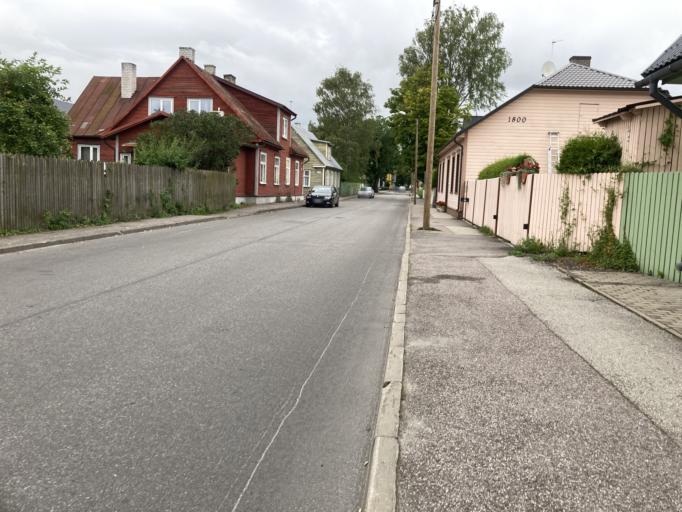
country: EE
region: Paernumaa
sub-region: Paernu linn
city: Parnu
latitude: 58.3794
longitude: 24.5092
